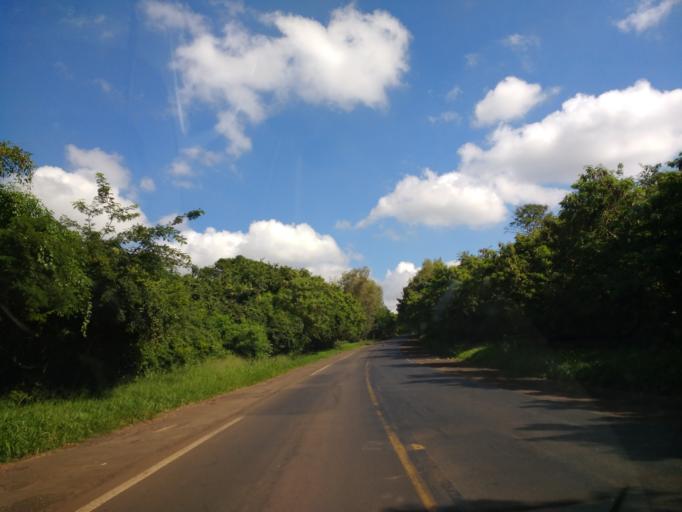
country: BR
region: Parana
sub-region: Umuarama
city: Umuarama
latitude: -23.8812
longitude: -53.3965
